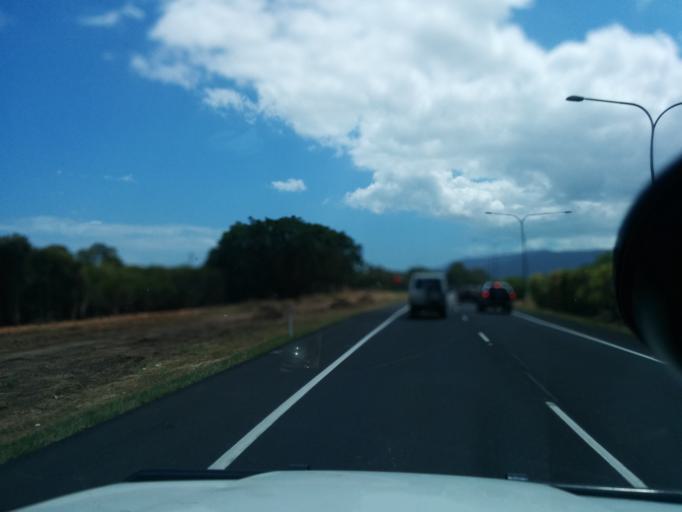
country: AU
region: Queensland
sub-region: Cairns
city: Woree
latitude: -16.9470
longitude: 145.7587
